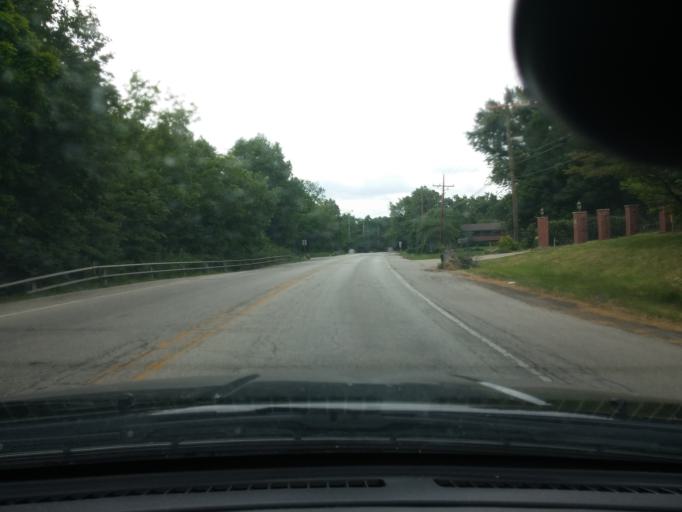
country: US
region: Indiana
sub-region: Tippecanoe County
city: West Lafayette
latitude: 40.4477
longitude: -86.8995
